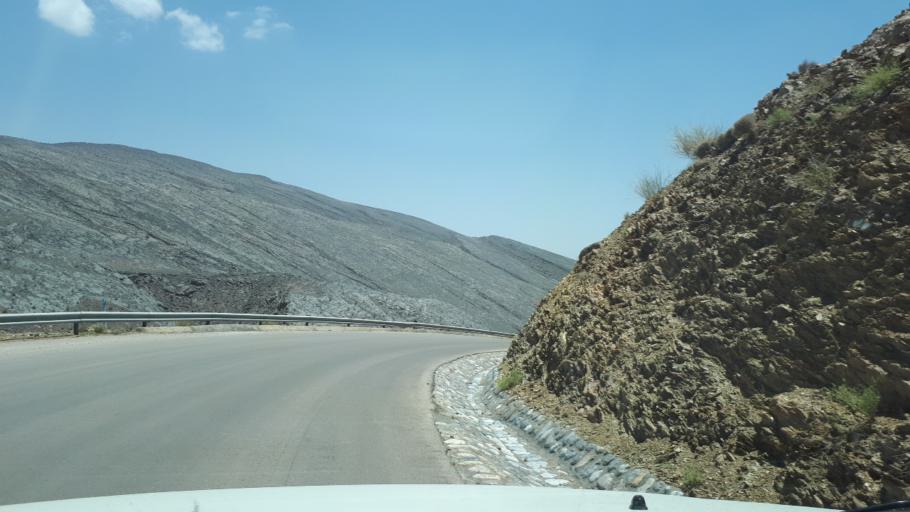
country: OM
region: Muhafazat ad Dakhiliyah
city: Bahla'
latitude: 23.2216
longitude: 57.1452
